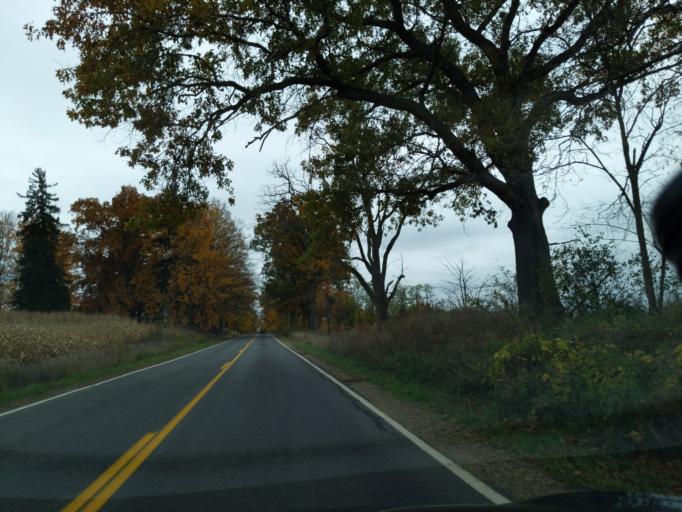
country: US
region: Michigan
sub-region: Jackson County
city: Spring Arbor
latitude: 42.3464
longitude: -84.6005
